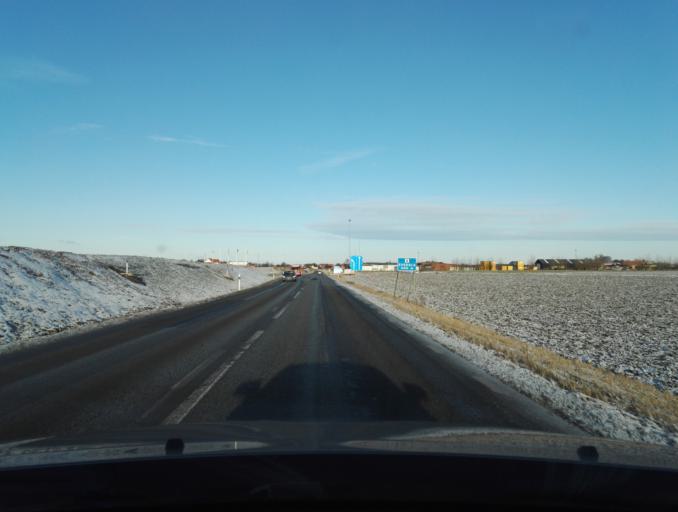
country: SE
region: Skane
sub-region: Svedala Kommun
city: Svedala
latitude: 55.4984
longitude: 13.2446
